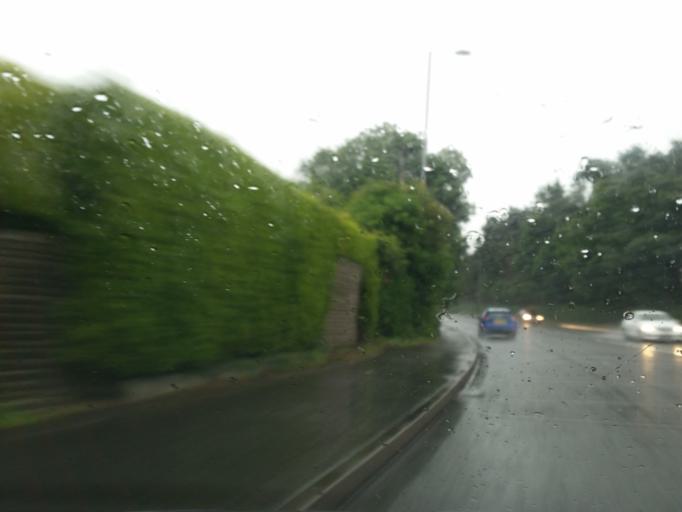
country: GB
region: Northern Ireland
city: Holywood
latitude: 54.6572
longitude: -5.7694
